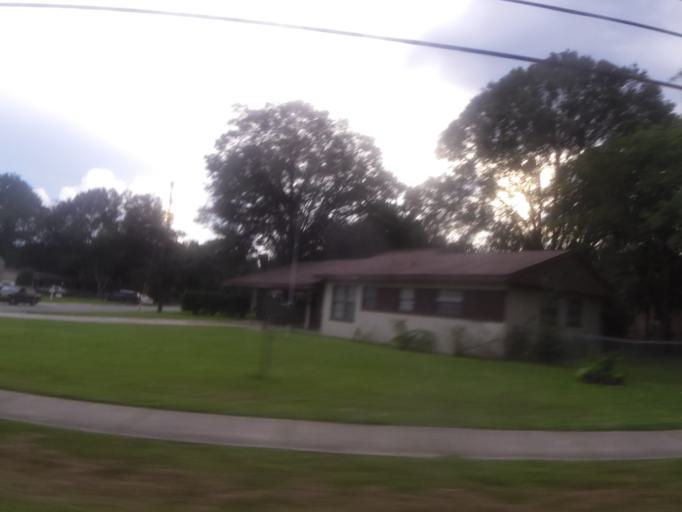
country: US
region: Florida
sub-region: Clay County
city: Bellair-Meadowbrook Terrace
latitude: 30.2843
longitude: -81.7848
